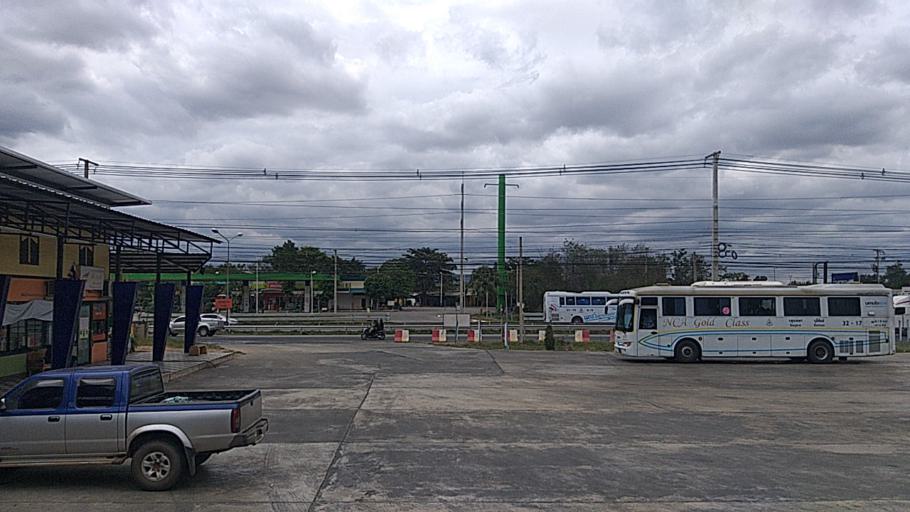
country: TH
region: Nakhon Ratchasima
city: Amphoe Sikhiu
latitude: 14.8428
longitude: 101.6211
